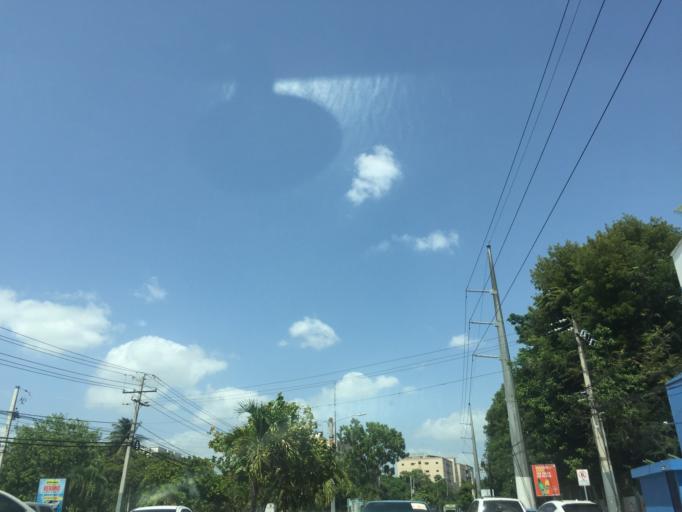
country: DO
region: Santiago
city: Santiago de los Caballeros
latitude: 19.4589
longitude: -70.6833
